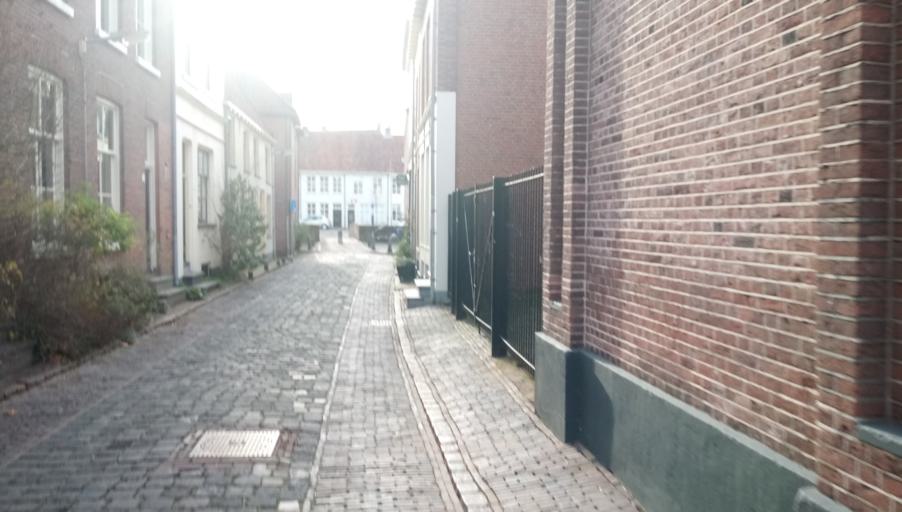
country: NL
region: Gelderland
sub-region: Gemeente Zutphen
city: Zutphen
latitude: 52.1435
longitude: 6.1983
